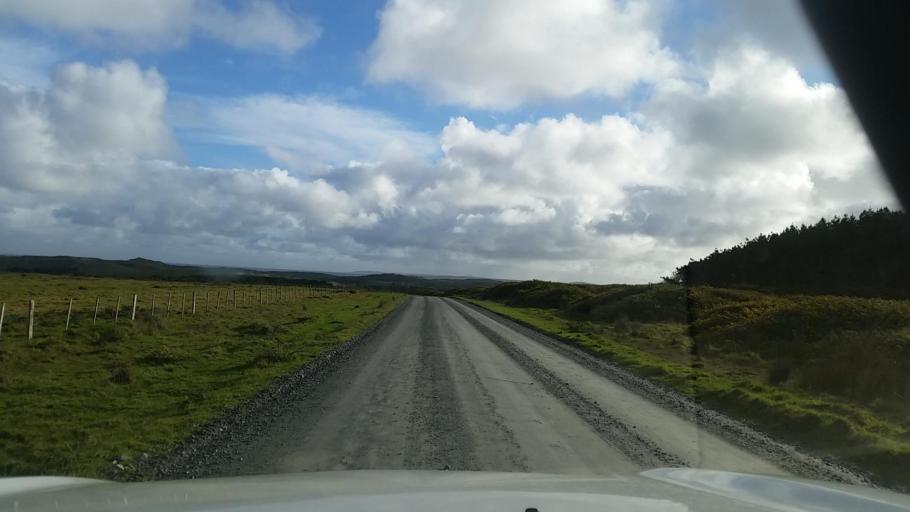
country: NZ
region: Chatham Islands
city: Waitangi
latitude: -43.8315
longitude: -176.5450
